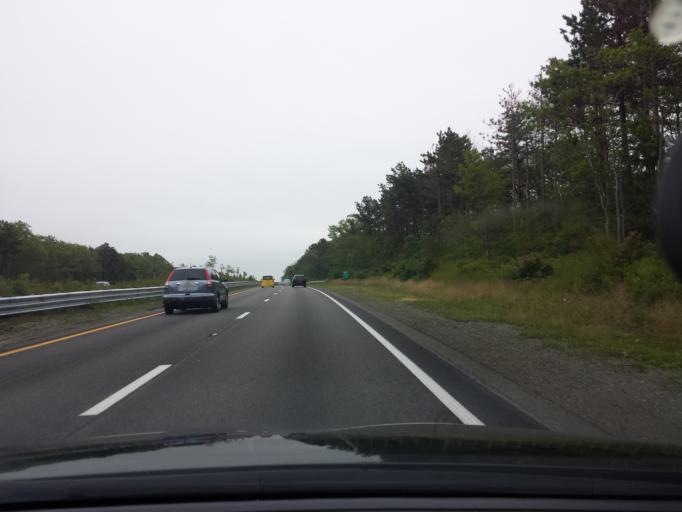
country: US
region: Massachusetts
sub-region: Barnstable County
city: East Sandwich
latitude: 41.7294
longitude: -70.4528
